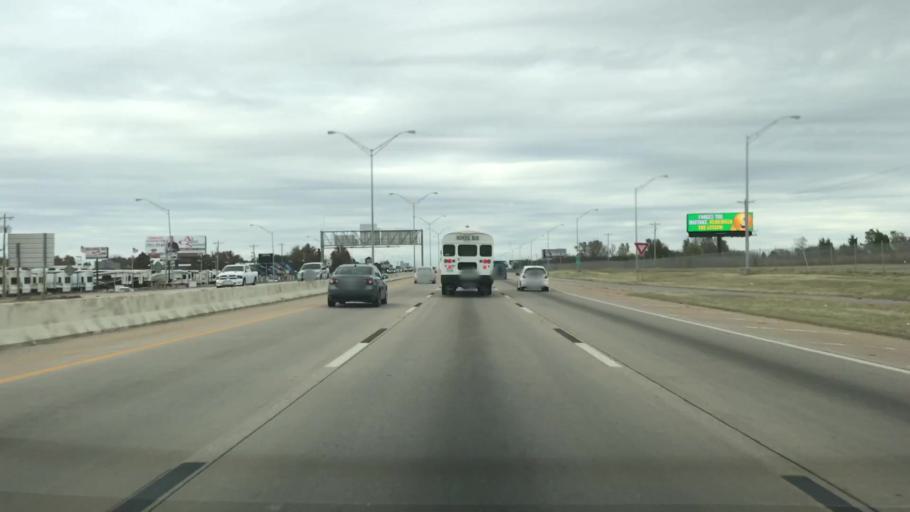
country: US
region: Oklahoma
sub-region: Cleveland County
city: Moore
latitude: 35.3660
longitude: -97.4948
